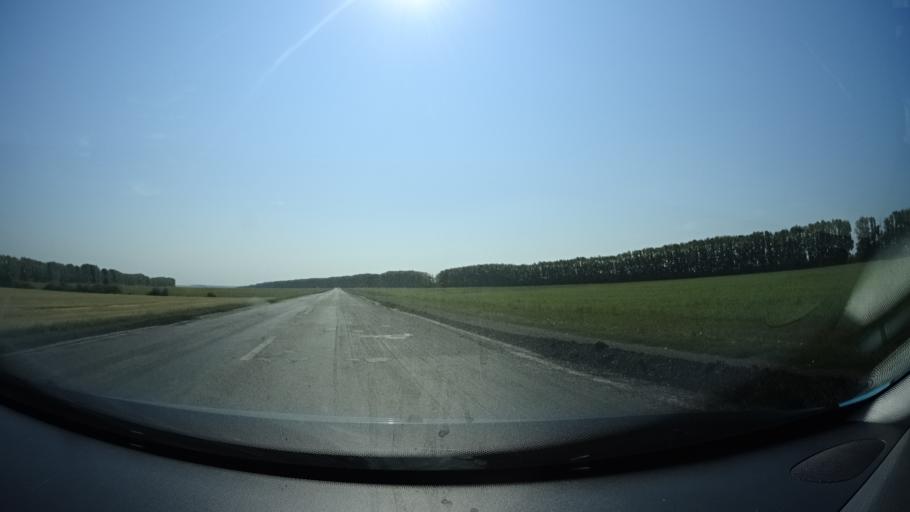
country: RU
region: Bashkortostan
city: Kabakovo
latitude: 54.4573
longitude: 55.9681
